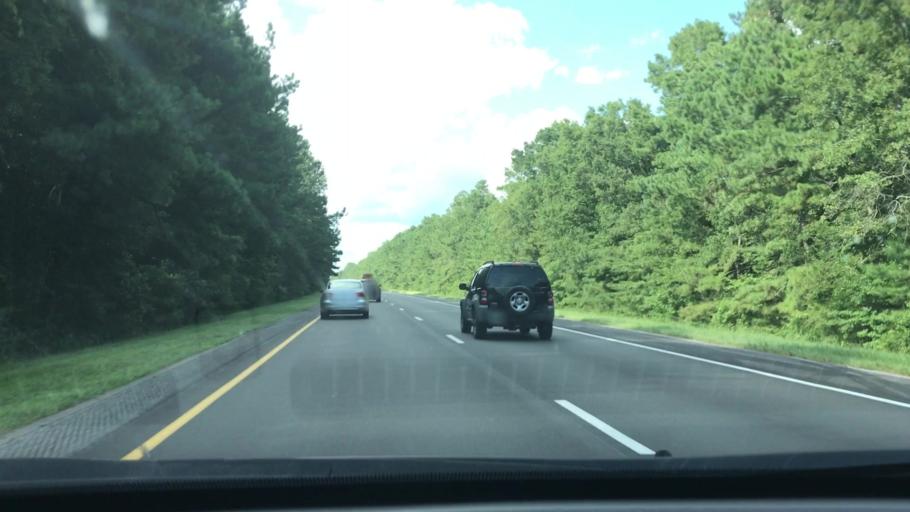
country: US
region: South Carolina
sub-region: Clarendon County
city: Manning
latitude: 33.7752
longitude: -80.1723
